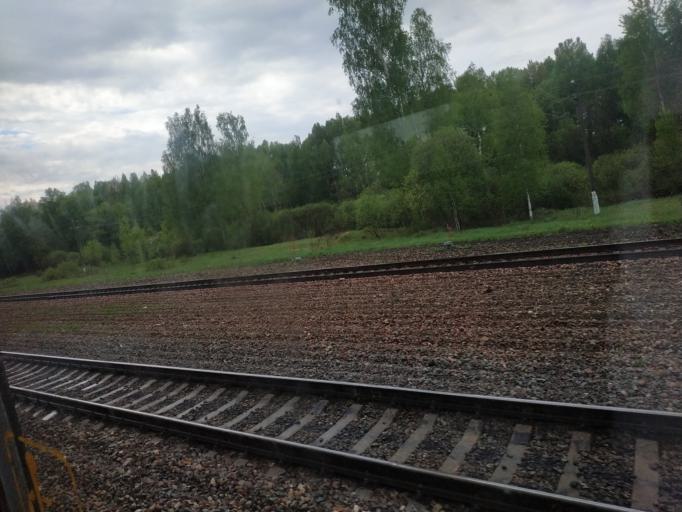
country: RU
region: Kaluga
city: Baryatino
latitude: 54.3525
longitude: 34.3254
